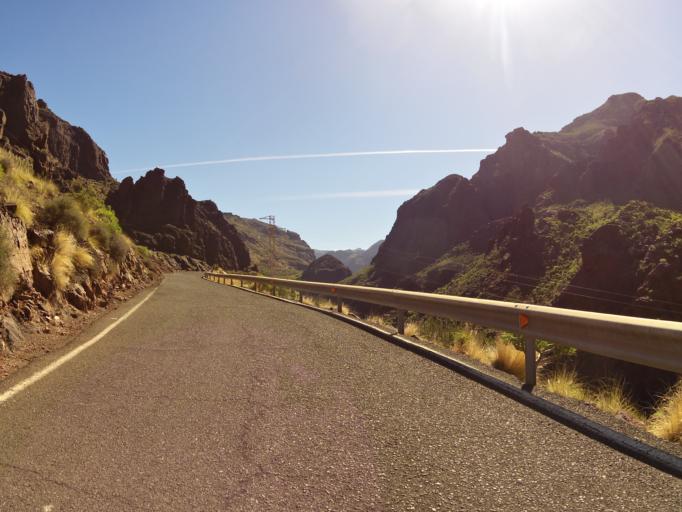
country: ES
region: Canary Islands
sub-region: Provincia de Las Palmas
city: San Nicolas
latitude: 27.9892
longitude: -15.7491
